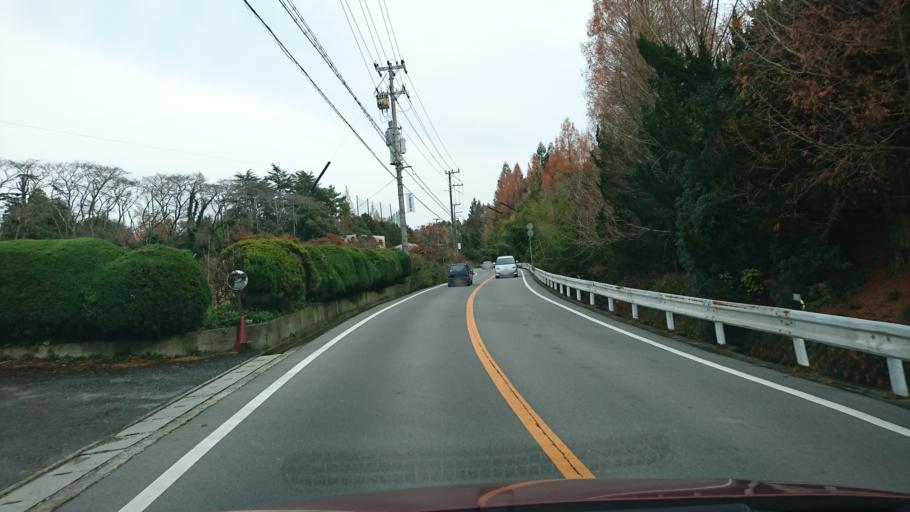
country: JP
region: Osaka
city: Ikeda
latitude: 34.8813
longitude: 135.4245
